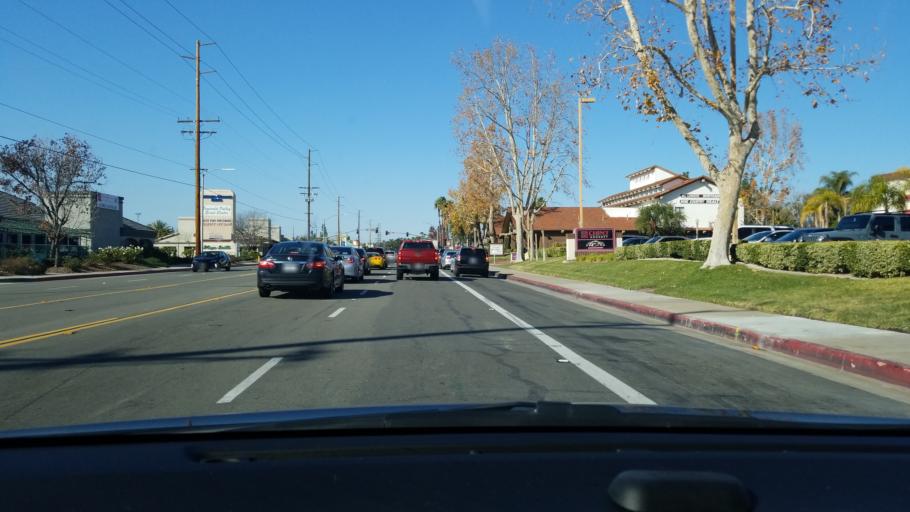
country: US
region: California
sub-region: Riverside County
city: Temecula
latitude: 33.5196
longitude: -117.1638
